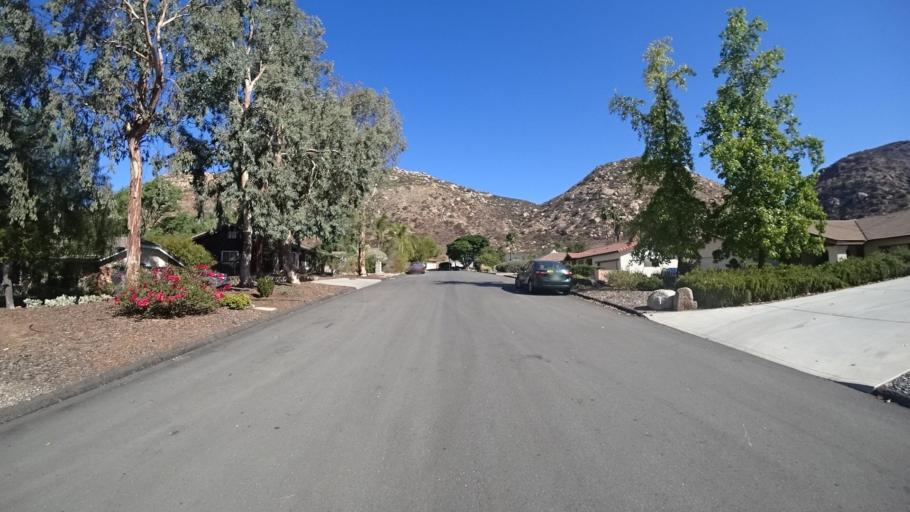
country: US
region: California
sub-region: San Diego County
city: San Diego Country Estates
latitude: 33.0028
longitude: -116.7603
